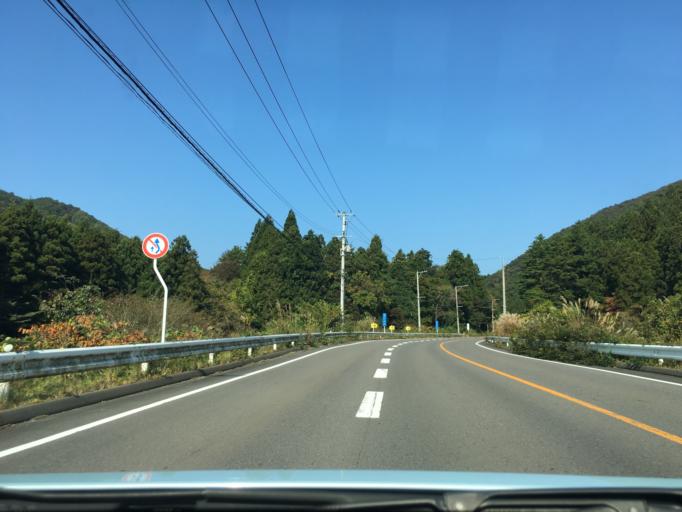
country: JP
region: Fukushima
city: Sukagawa
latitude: 37.2954
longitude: 140.1611
